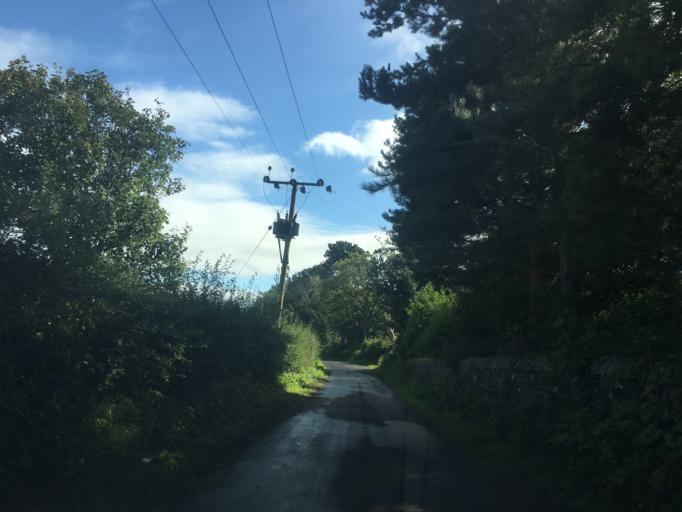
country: GB
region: Scotland
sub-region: Edinburgh
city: Kirkliston
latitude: 55.9558
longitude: -3.3731
